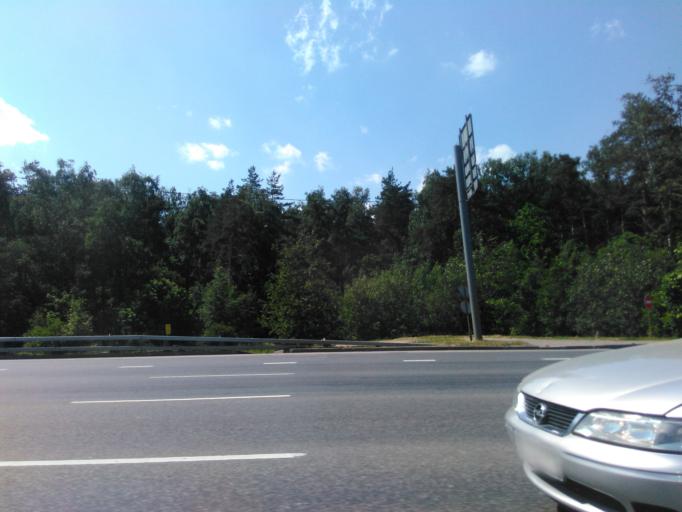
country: RU
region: Moskovskaya
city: Kotel'niki
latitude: 55.6596
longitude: 37.8398
